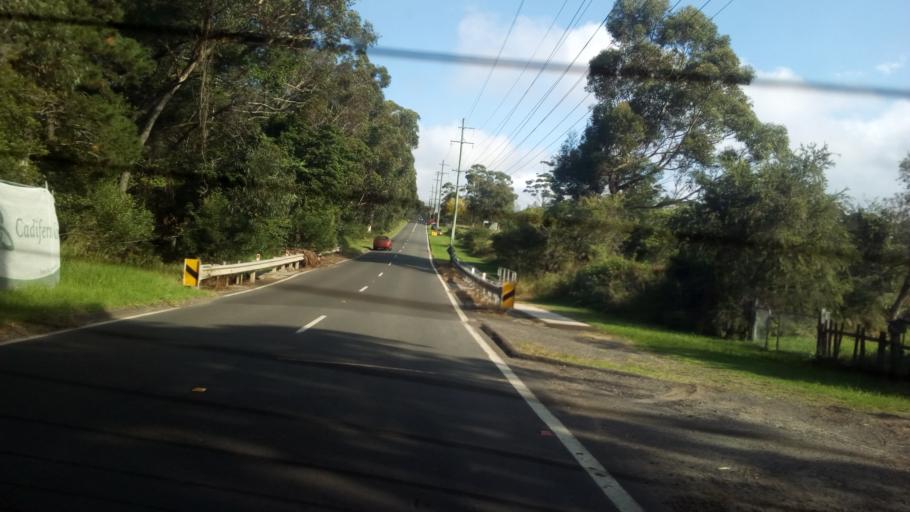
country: AU
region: New South Wales
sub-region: Wollongong
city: Helensburgh
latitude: -34.2080
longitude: 150.9782
